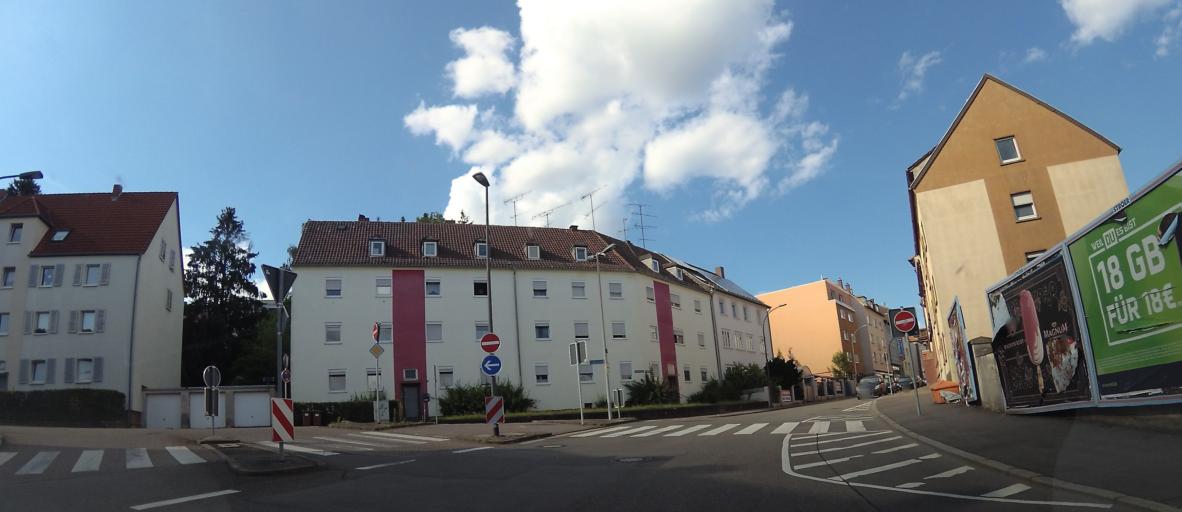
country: DE
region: Rheinland-Pfalz
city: Pirmasens
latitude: 49.1927
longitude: 7.6072
